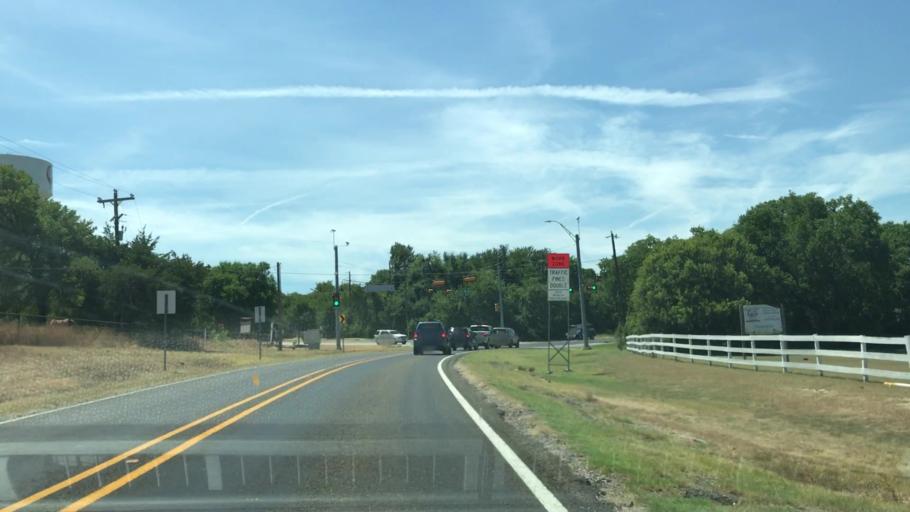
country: US
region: Texas
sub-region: Collin County
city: Fairview
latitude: 33.1323
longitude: -96.6095
